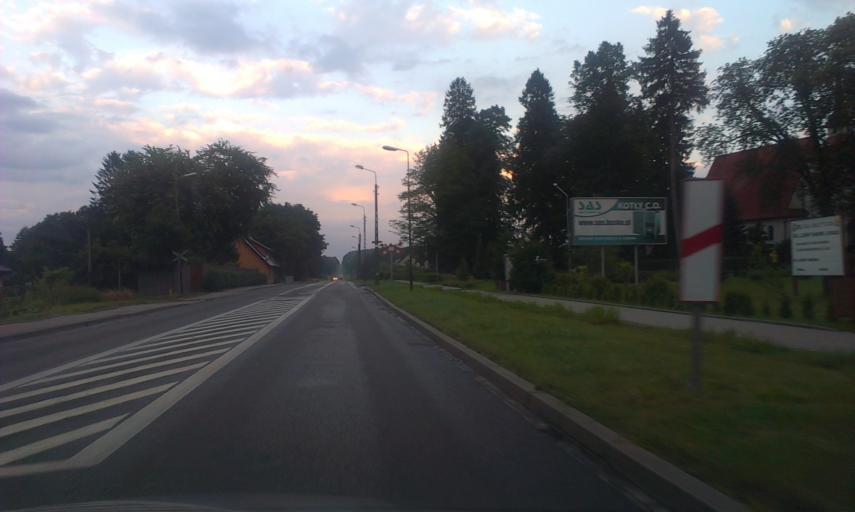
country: PL
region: West Pomeranian Voivodeship
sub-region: Powiat koszalinski
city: Sianow
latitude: 54.1254
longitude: 16.3015
